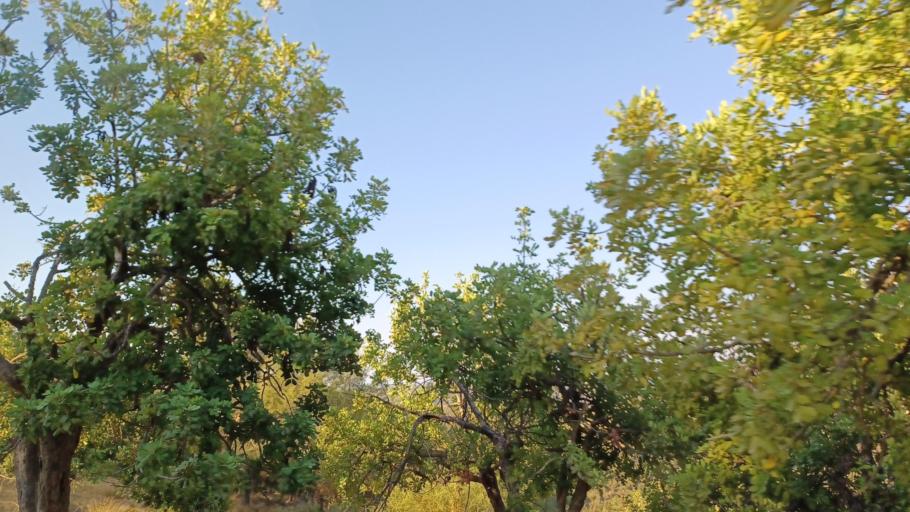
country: CY
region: Limassol
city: Pissouri
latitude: 34.7280
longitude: 32.6672
